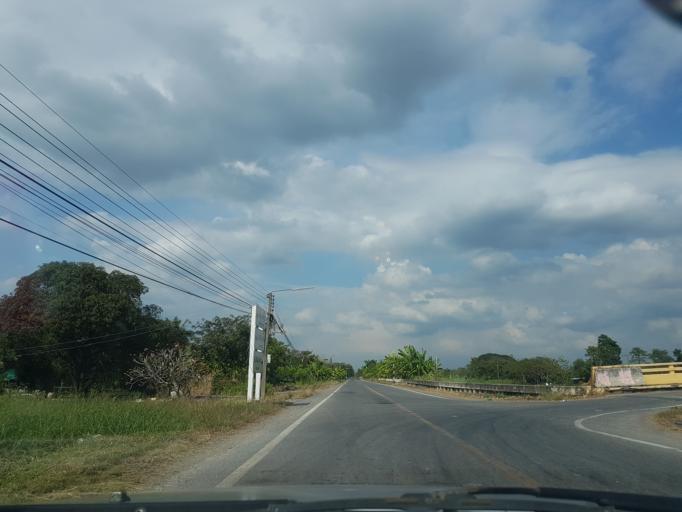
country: TH
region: Pathum Thani
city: Nong Suea
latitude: 14.1563
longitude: 100.8915
